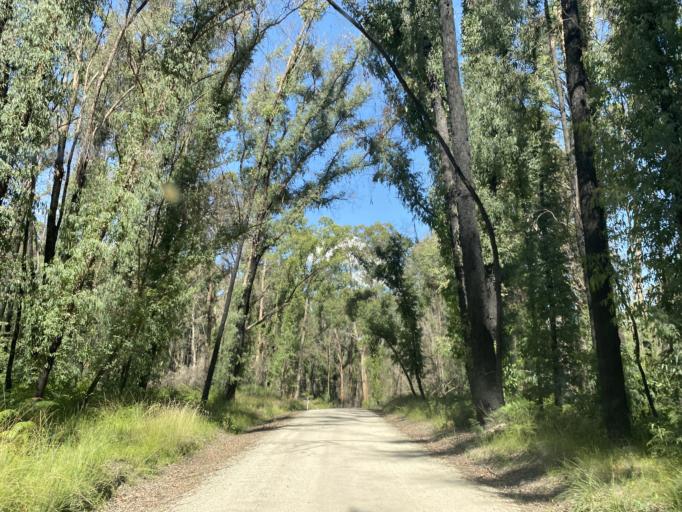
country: AU
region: Victoria
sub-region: Cardinia
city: Gembrook
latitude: -37.9829
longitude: 145.6379
